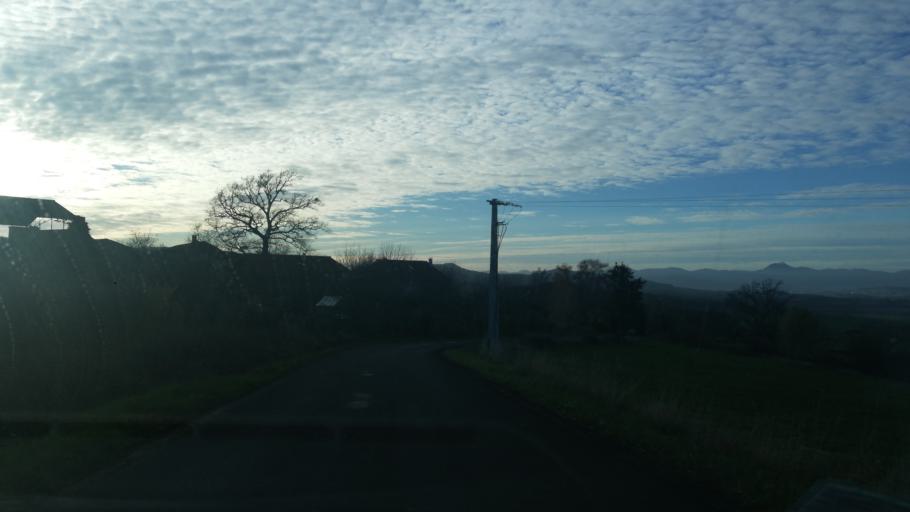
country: FR
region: Auvergne
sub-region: Departement du Puy-de-Dome
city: Billom
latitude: 45.7004
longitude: 3.3565
